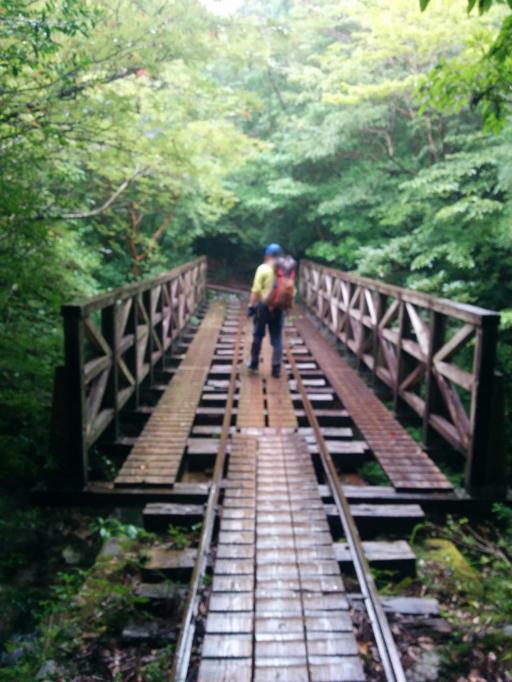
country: JP
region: Kagoshima
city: Nishinoomote
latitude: 30.3544
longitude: 130.5624
